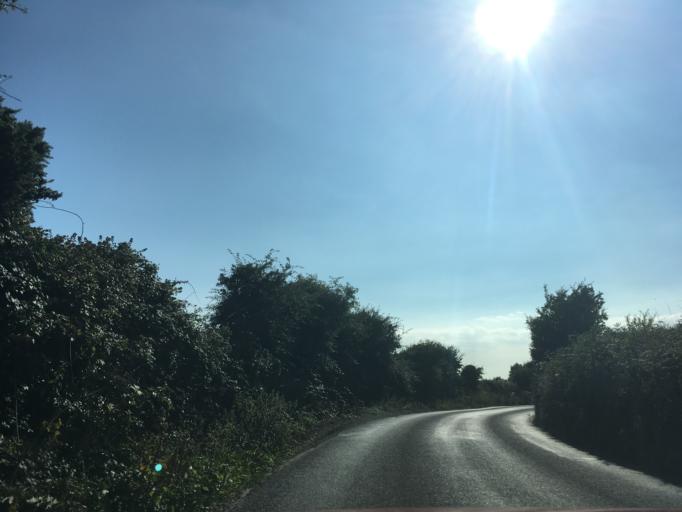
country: IE
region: Leinster
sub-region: Loch Garman
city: Rosslare
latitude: 52.2253
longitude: -6.4476
